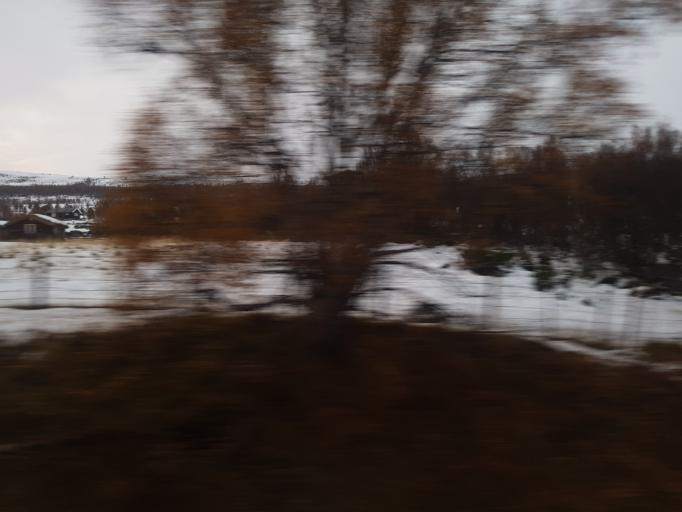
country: NO
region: Oppland
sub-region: Dovre
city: Dovre
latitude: 62.1653
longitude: 9.3833
